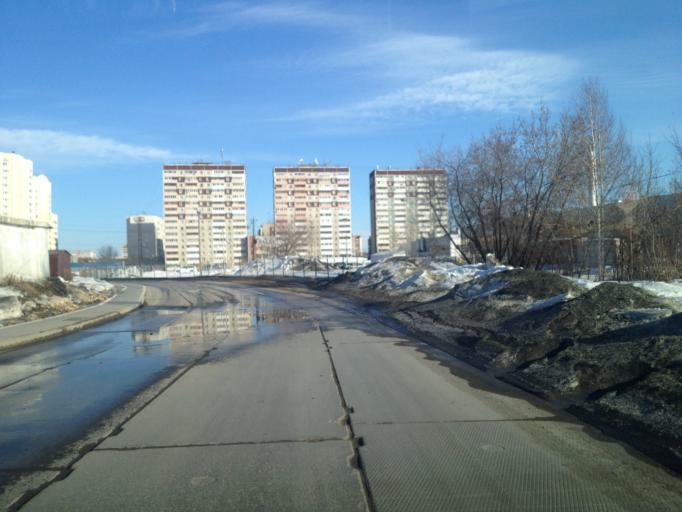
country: RU
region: Sverdlovsk
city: Shirokaya Rechka
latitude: 56.8292
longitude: 60.5250
